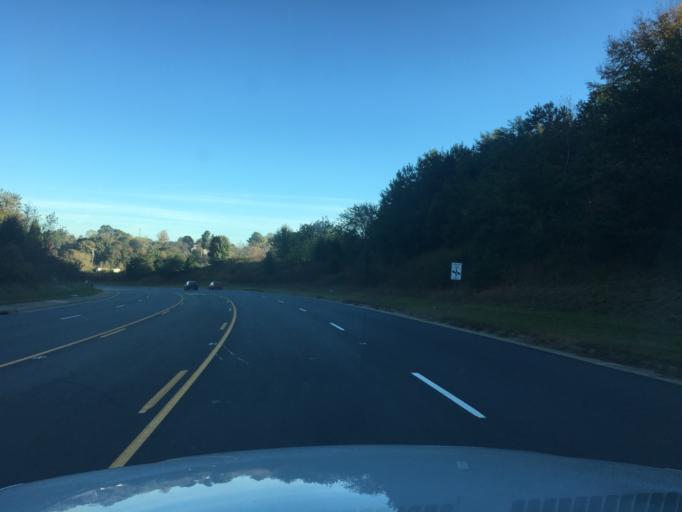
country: US
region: North Carolina
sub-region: Catawba County
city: Mountain View
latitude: 35.6971
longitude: -81.3476
